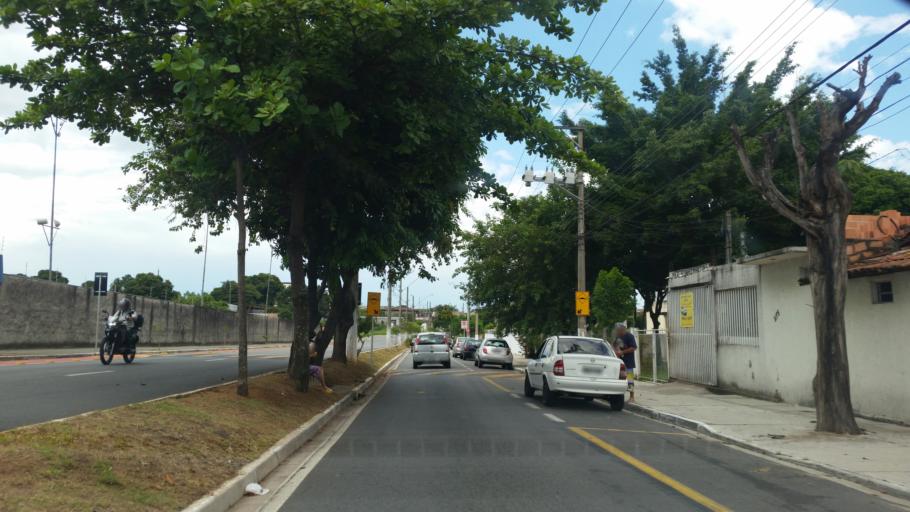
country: BR
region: Sao Paulo
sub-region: Taubate
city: Taubate
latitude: -23.0220
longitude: -45.5762
